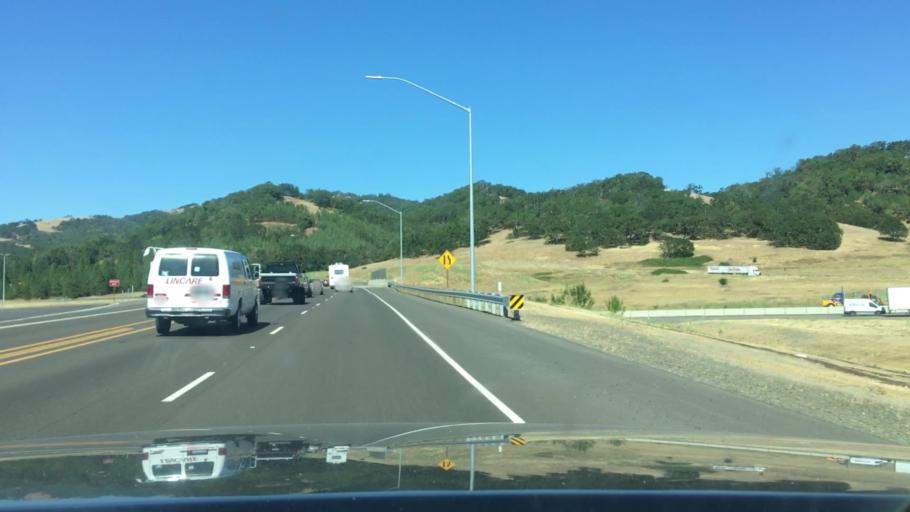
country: US
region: Oregon
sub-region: Douglas County
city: Green
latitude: 43.1520
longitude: -123.3668
